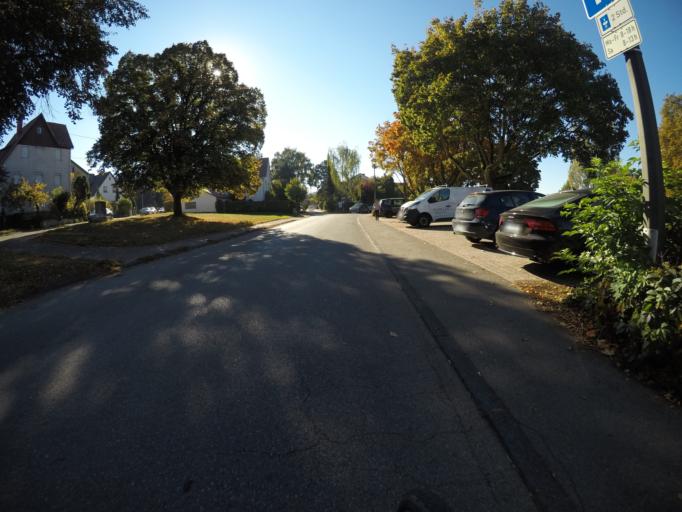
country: DE
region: Baden-Wuerttemberg
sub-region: Regierungsbezirk Stuttgart
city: Filderstadt
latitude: 48.6488
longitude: 9.2193
